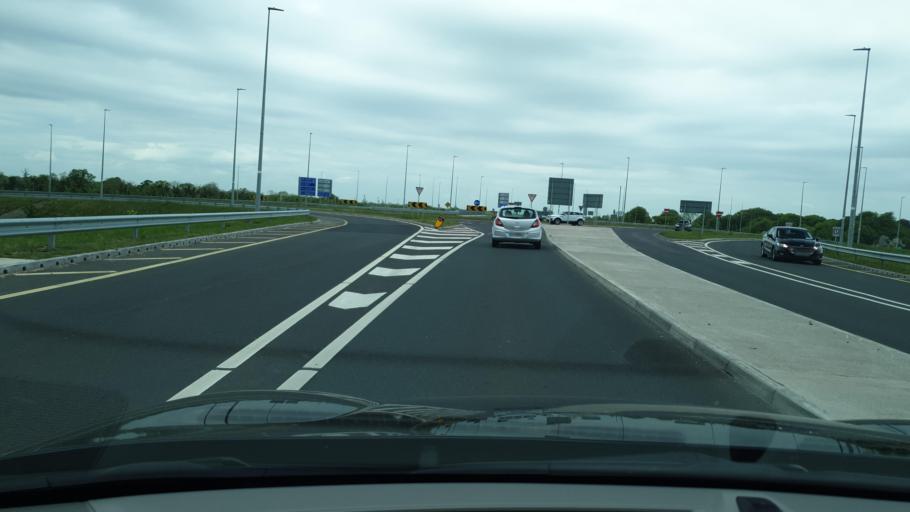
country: IE
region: Leinster
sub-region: Kildare
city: Sallins
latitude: 53.2330
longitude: -6.6835
